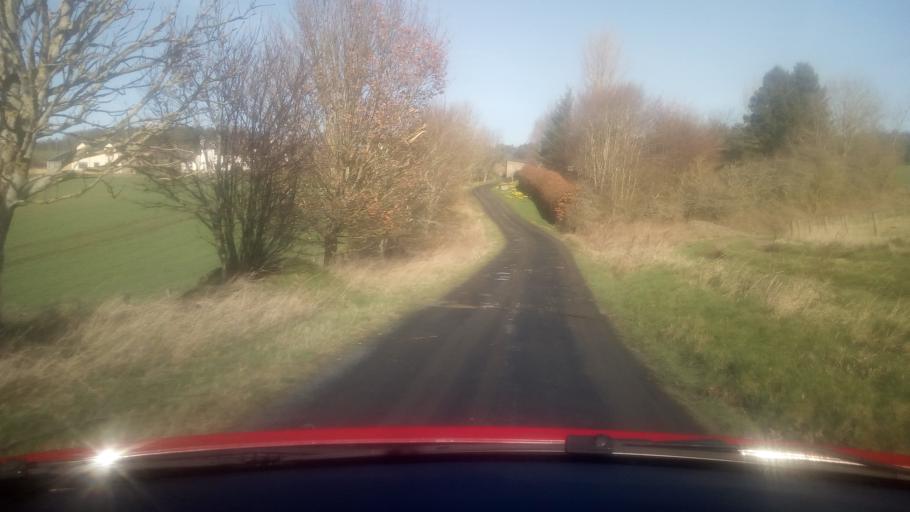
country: GB
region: Scotland
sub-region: The Scottish Borders
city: Jedburgh
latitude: 55.5184
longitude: -2.5707
